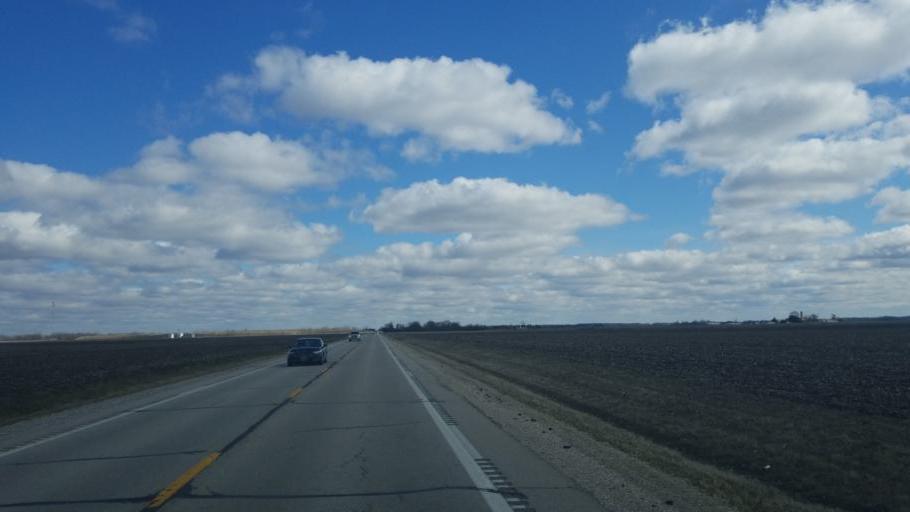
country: US
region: Illinois
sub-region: Douglas County
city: Villa Grove
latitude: 39.7921
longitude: -88.0789
